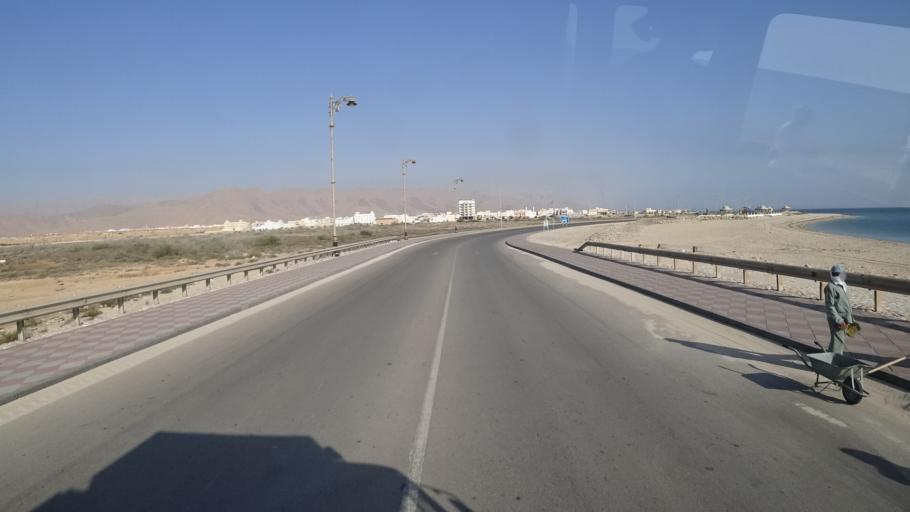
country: OM
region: Ash Sharqiyah
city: Sur
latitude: 22.5980
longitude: 59.4874
